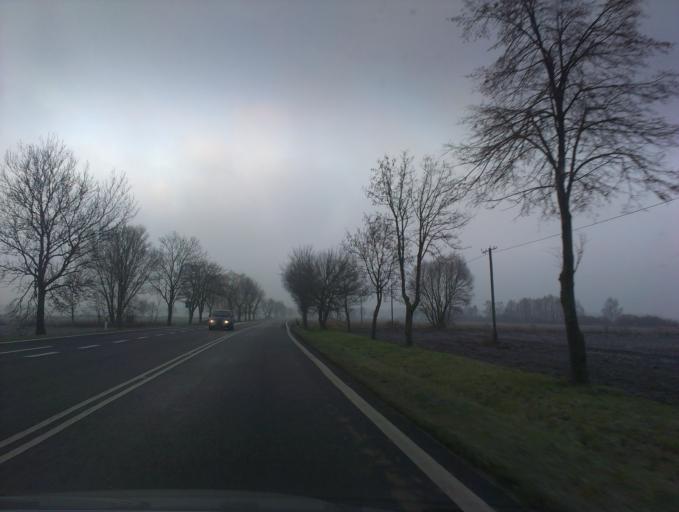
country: PL
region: Greater Poland Voivodeship
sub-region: Powiat chodzieski
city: Budzyn
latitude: 52.8688
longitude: 16.9760
